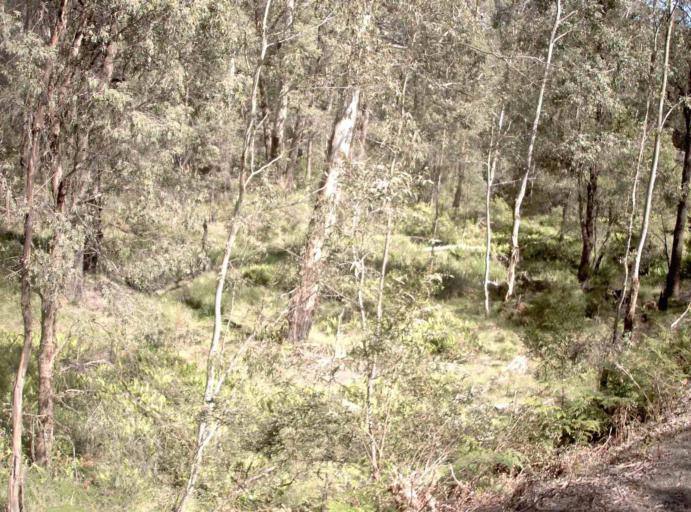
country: AU
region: New South Wales
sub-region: Bombala
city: Bombala
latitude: -37.1472
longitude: 148.7242
